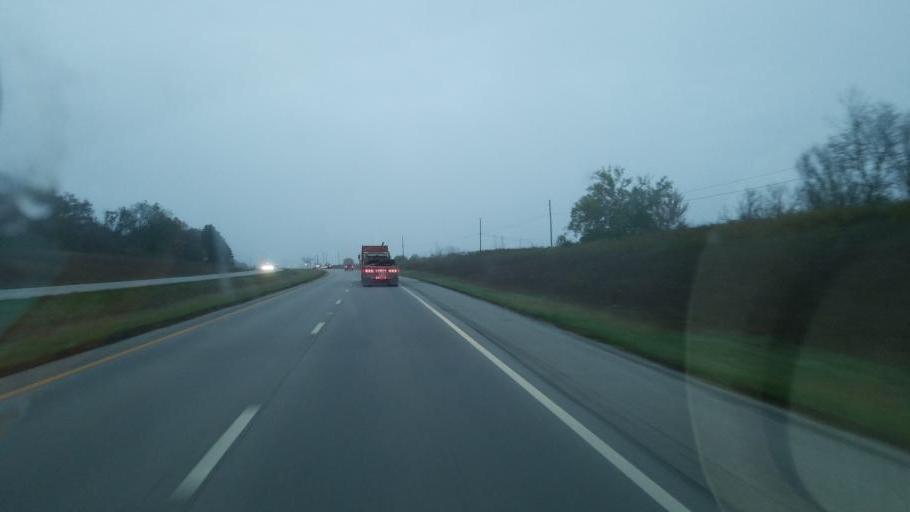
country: US
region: Ohio
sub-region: Pike County
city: Piketon
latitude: 39.0274
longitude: -83.0271
